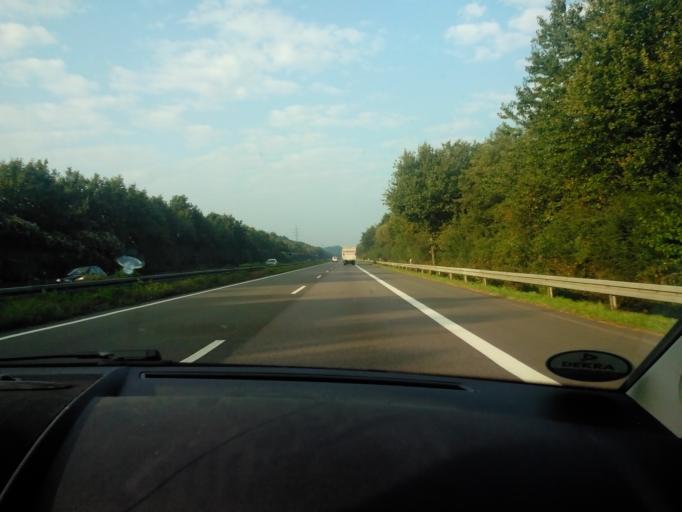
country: DE
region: Saarland
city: Heusweiler
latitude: 49.3338
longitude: 6.8948
